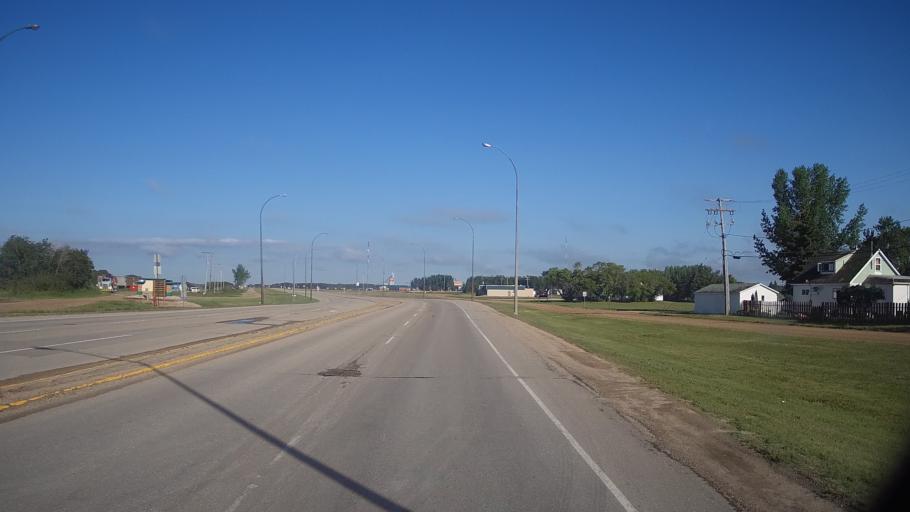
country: CA
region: Saskatchewan
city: Lanigan
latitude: 51.8464
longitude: -105.0383
